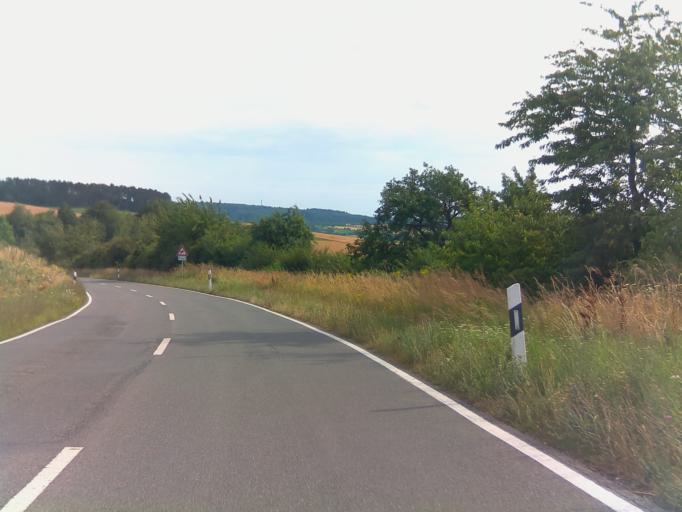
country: DE
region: Baden-Wuerttemberg
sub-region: Karlsruhe Region
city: Walldurn
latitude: 49.5210
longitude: 9.4026
